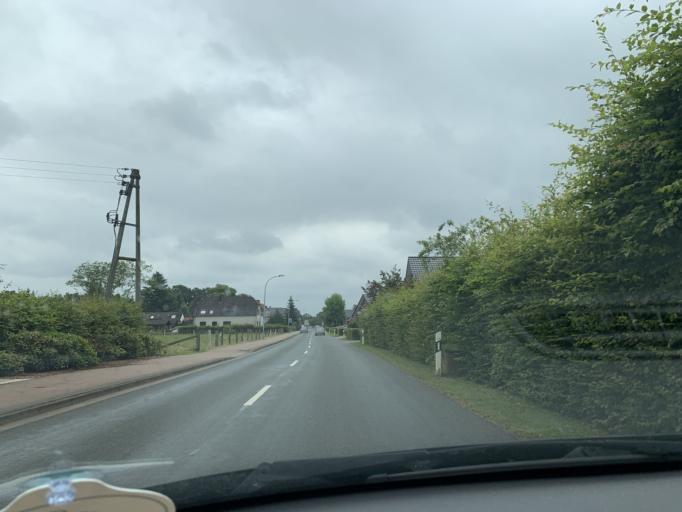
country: DE
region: North Rhine-Westphalia
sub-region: Regierungsbezirk Munster
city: Ostbevern
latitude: 52.1119
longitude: 7.8528
